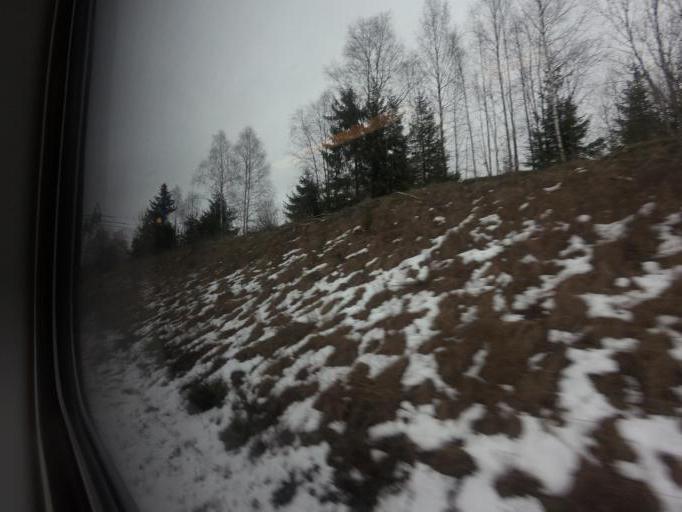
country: NO
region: Akershus
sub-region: Eidsvoll
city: Eidsvoll
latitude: 60.3869
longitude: 11.2350
